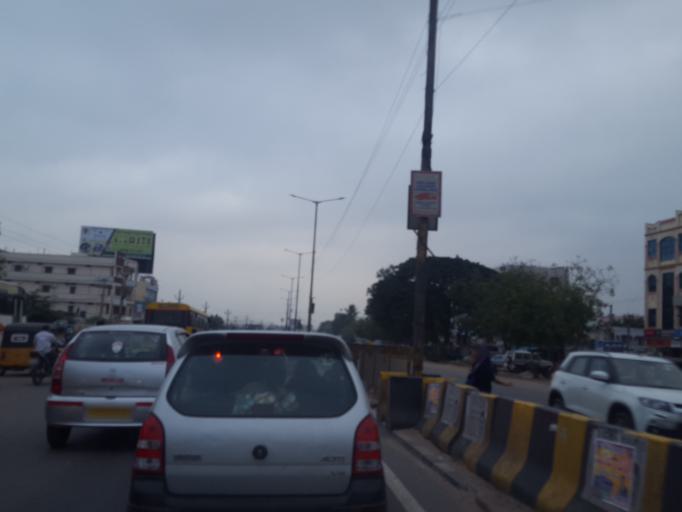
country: IN
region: Telangana
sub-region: Medak
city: Serilingampalle
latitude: 17.5137
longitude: 78.2881
